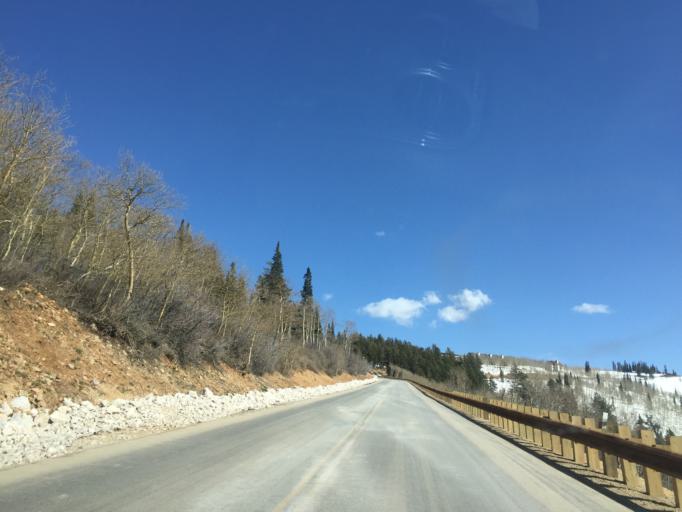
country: US
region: Utah
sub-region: Weber County
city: Wolf Creek
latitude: 41.3746
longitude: -111.7748
